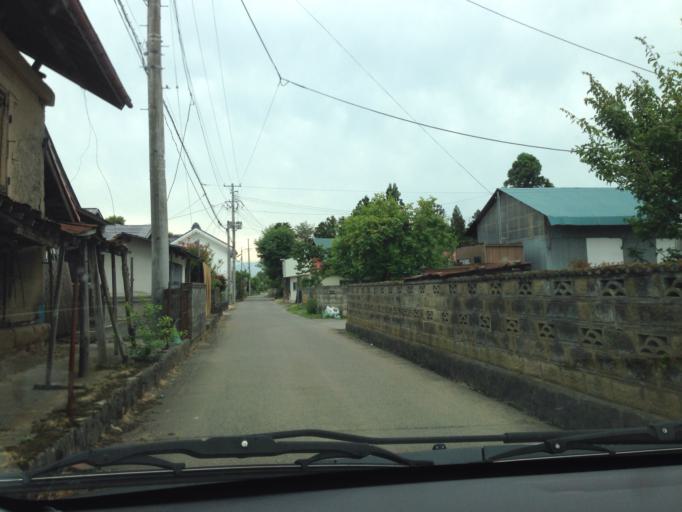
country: JP
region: Fukushima
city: Kitakata
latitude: 37.5330
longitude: 139.8972
